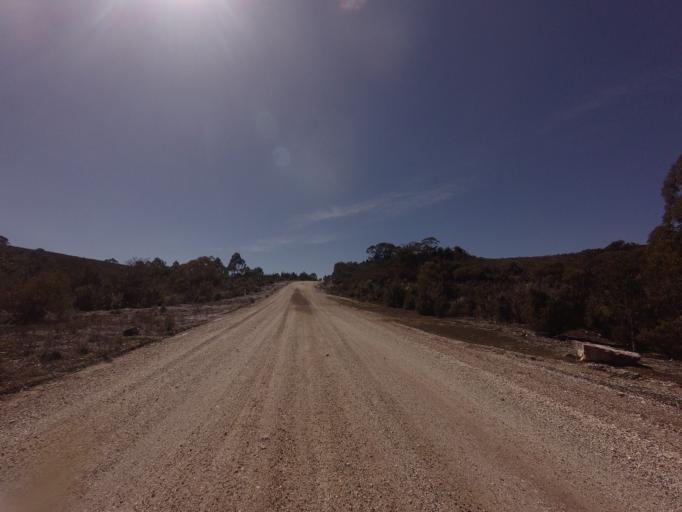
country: AU
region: Tasmania
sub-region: Huon Valley
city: Geeveston
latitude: -43.0326
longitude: 146.2982
